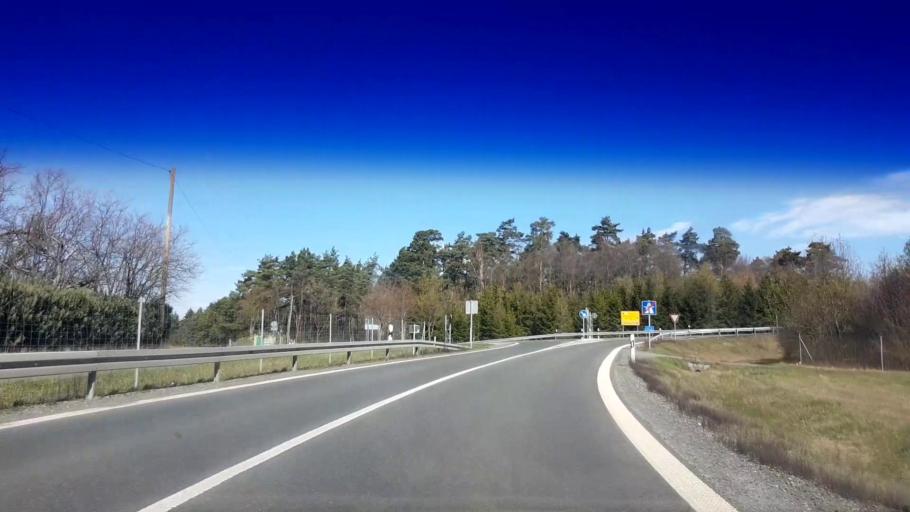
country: DE
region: Bavaria
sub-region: Upper Franconia
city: Bindlach
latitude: 50.0139
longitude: 11.6043
